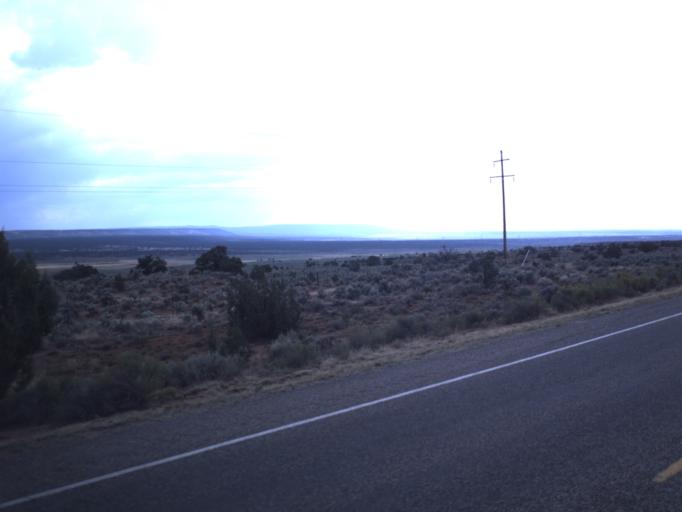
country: US
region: Utah
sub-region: Kane County
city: Kanab
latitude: 37.0458
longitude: -112.2109
